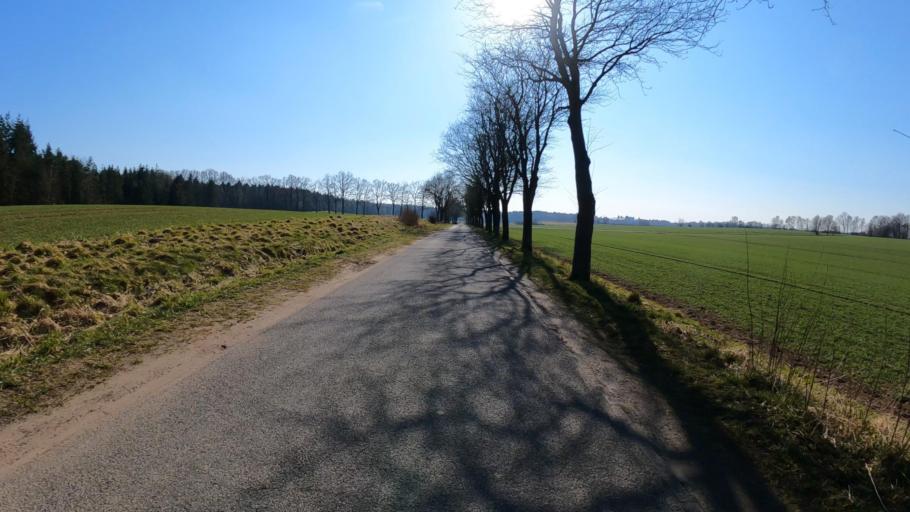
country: DE
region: Lower Saxony
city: Bendestorf
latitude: 53.3477
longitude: 9.9186
